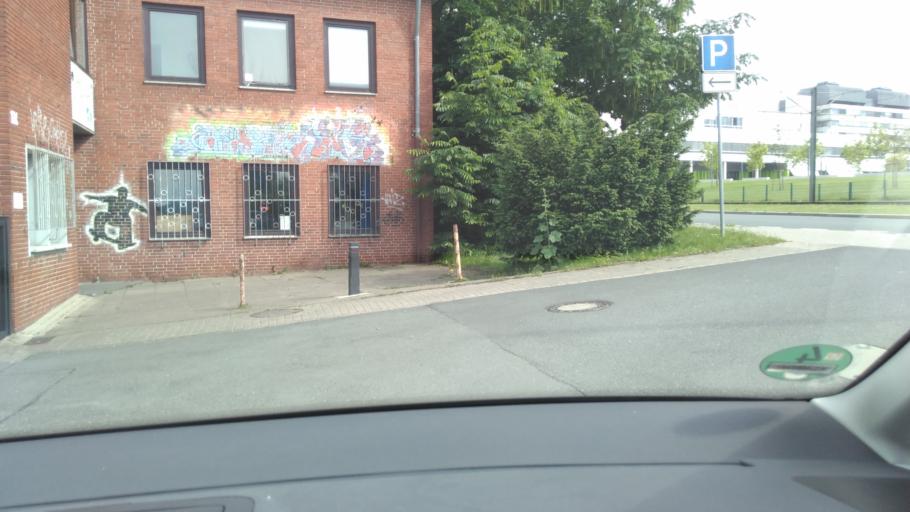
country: DE
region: North Rhine-Westphalia
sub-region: Regierungsbezirk Detmold
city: Bielefeld
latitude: 52.0420
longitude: 8.4915
